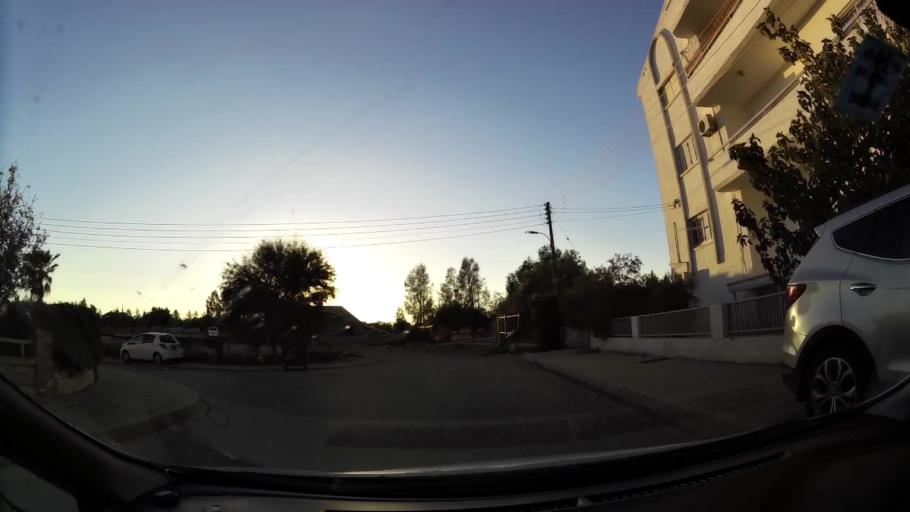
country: CY
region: Lefkosia
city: Nicosia
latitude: 35.2053
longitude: 33.3268
